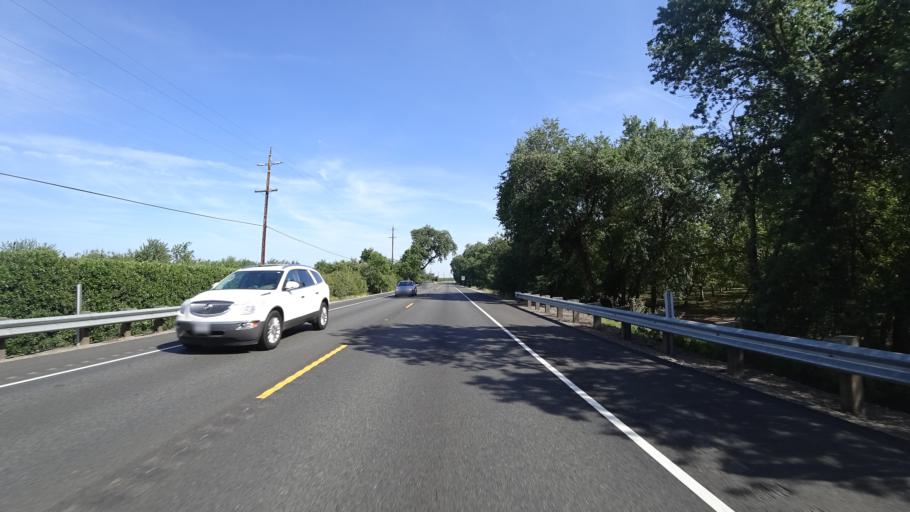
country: US
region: California
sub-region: Glenn County
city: Hamilton City
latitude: 39.8824
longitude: -121.9751
